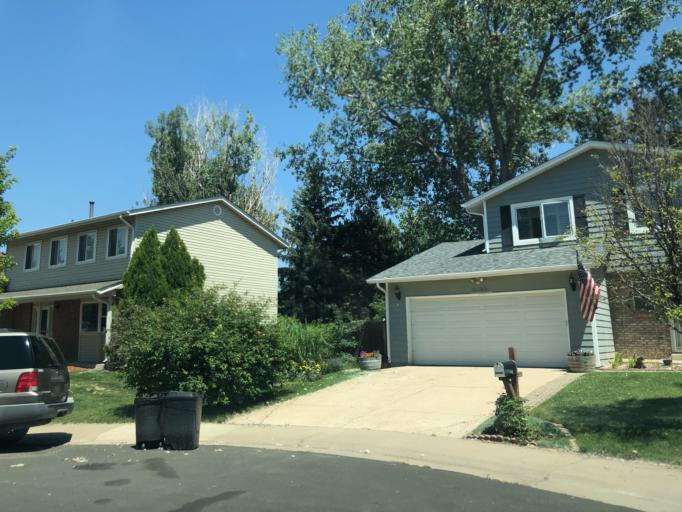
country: US
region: Colorado
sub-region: Arapahoe County
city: Dove Valley
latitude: 39.6224
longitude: -104.7810
